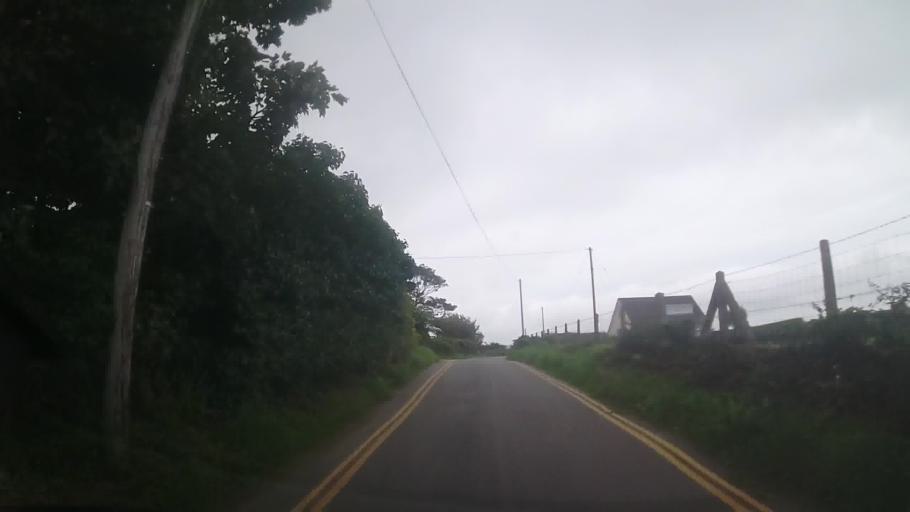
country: GB
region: Wales
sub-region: Gwynedd
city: Caernarfon
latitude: 53.1607
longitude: -4.3692
